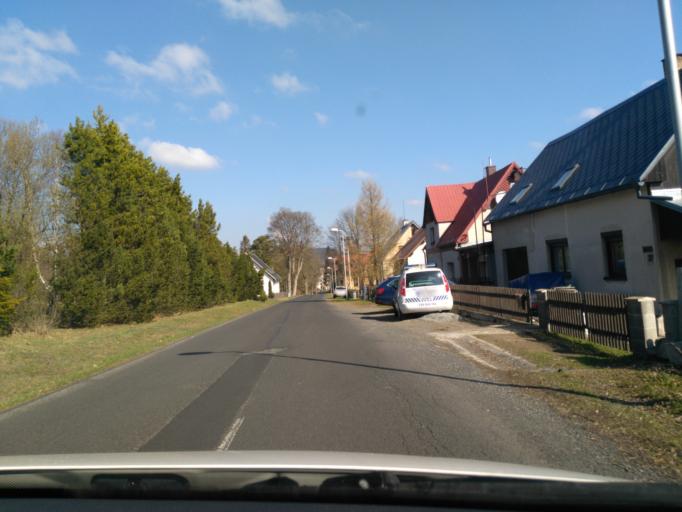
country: CZ
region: Ustecky
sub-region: Okres Chomutov
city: Vejprty
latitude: 50.4793
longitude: 13.0332
